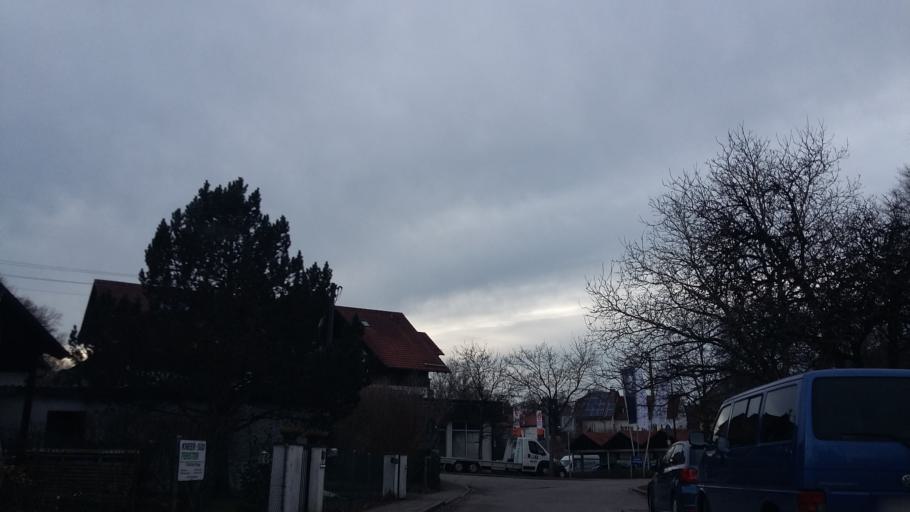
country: DE
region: Bavaria
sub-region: Upper Bavaria
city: Wessling
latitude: 48.0785
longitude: 11.2587
